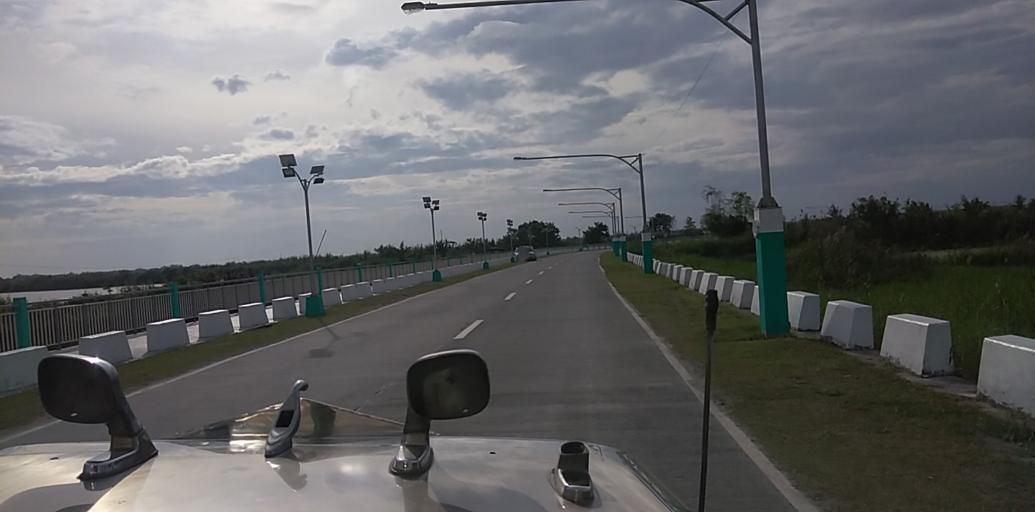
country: PH
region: Central Luzon
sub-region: Province of Pampanga
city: Minalin
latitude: 14.9745
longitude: 120.6852
